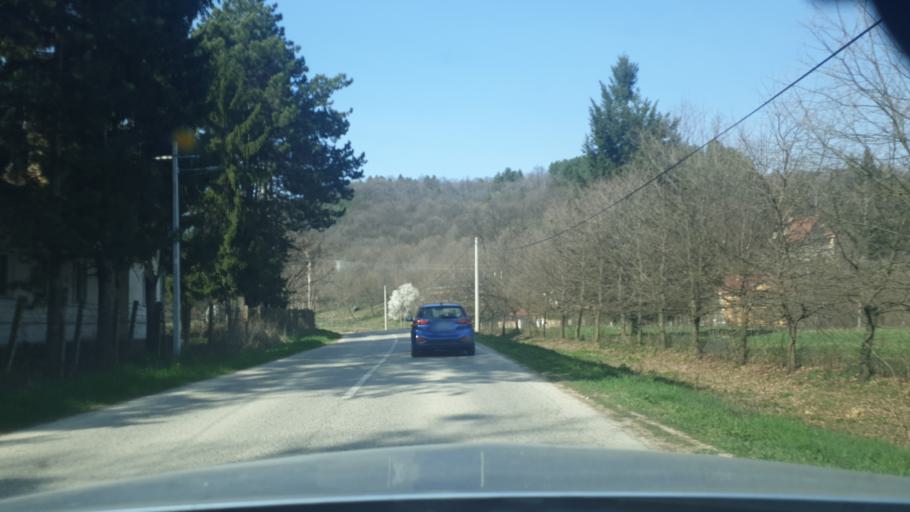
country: RS
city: Vrdnik
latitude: 45.1324
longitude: 19.7825
